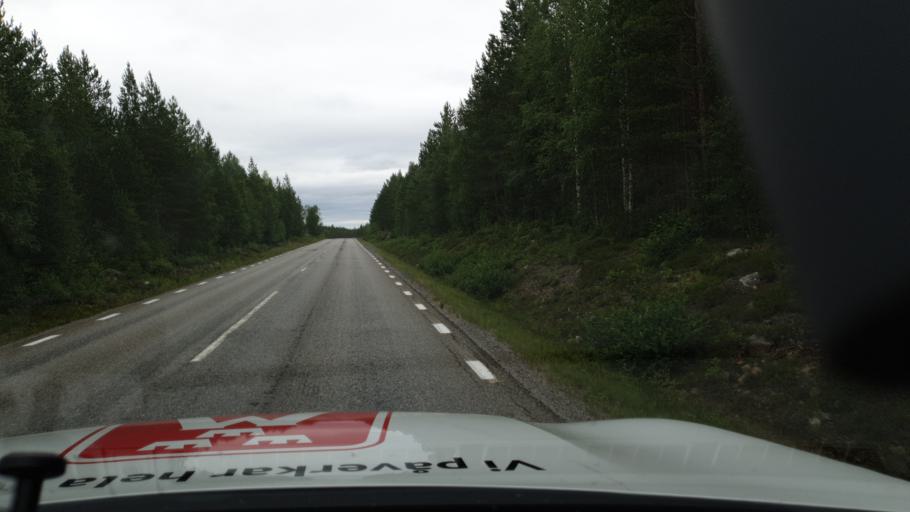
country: SE
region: Vaesterbotten
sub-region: Umea Kommun
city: Saevar
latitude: 64.0557
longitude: 20.4876
